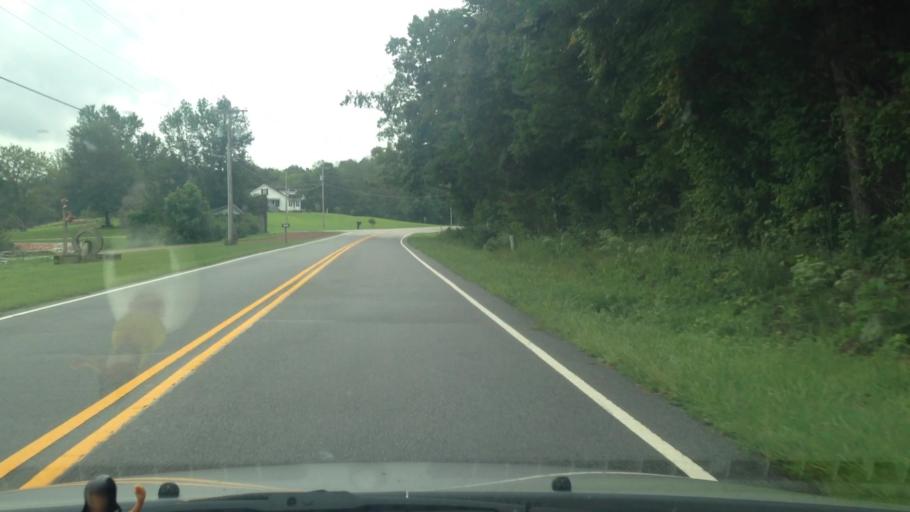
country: US
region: North Carolina
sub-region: Stokes County
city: Danbury
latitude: 36.4121
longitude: -80.1128
